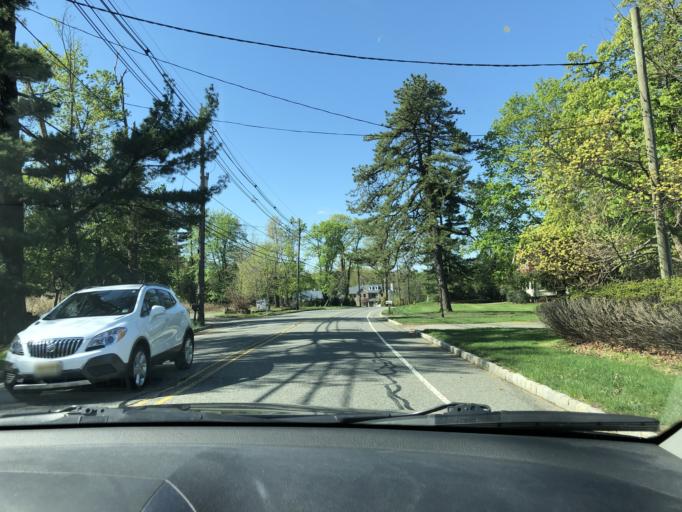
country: US
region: New Jersey
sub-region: Essex County
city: North Caldwell
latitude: 40.8731
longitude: -74.2608
